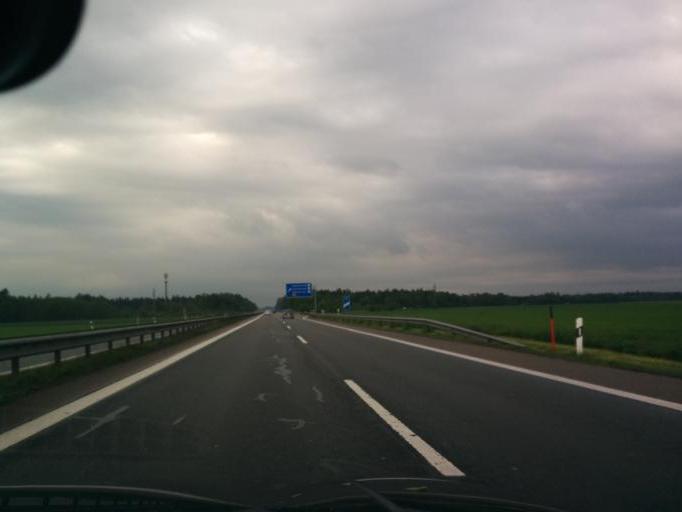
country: DE
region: Bavaria
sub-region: Upper Bavaria
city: Ottobrunn
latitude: 48.0453
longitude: 11.6484
